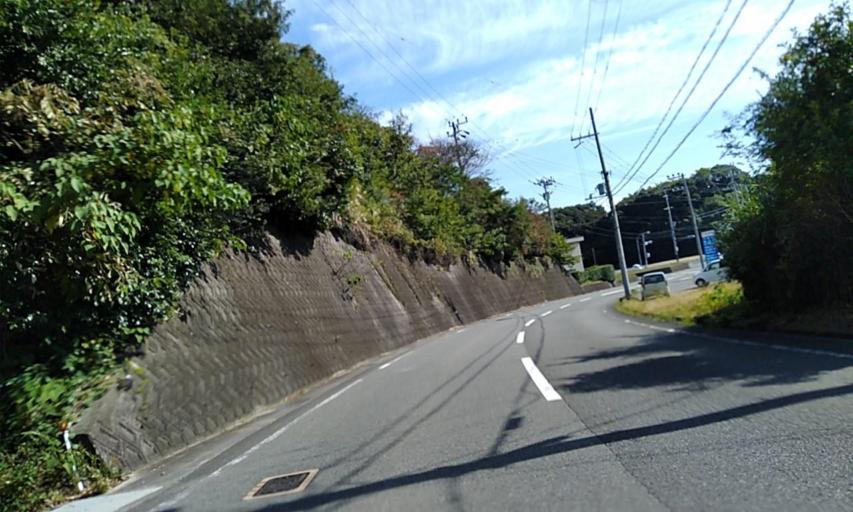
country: JP
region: Wakayama
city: Gobo
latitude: 33.8893
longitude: 135.1768
